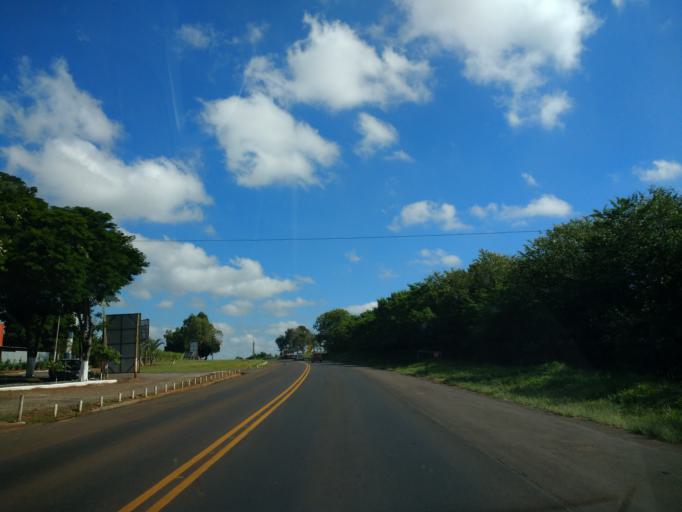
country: BR
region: Parana
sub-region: Umuarama
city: Umuarama
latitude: -23.8306
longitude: -53.3529
